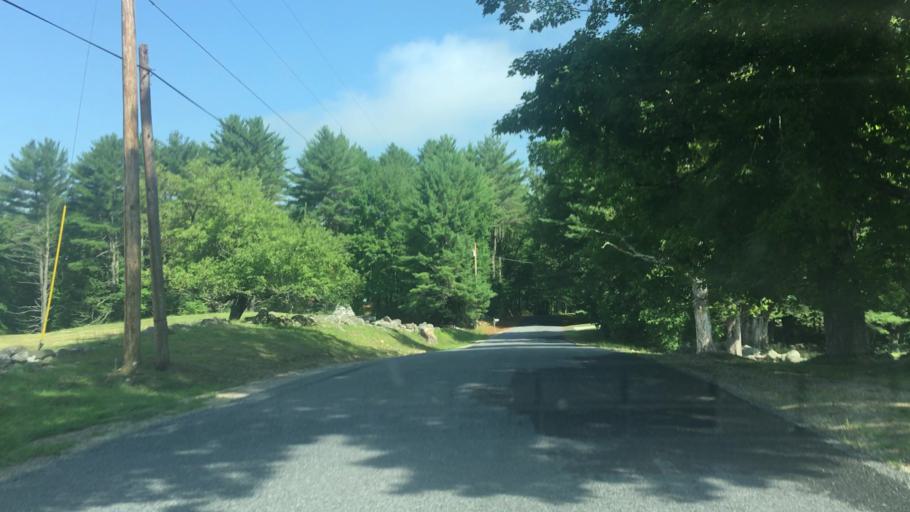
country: US
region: Maine
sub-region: Oxford County
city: Paris
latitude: 44.2907
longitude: -70.5243
